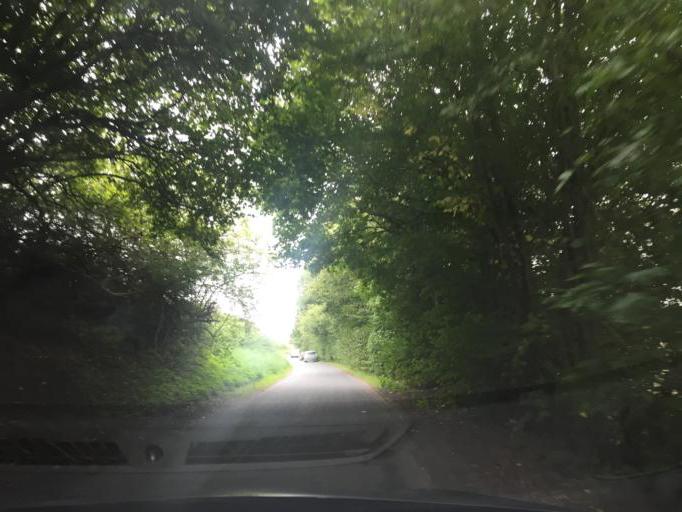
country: DK
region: South Denmark
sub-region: Assens Kommune
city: Tommerup
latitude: 55.3614
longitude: 10.2183
